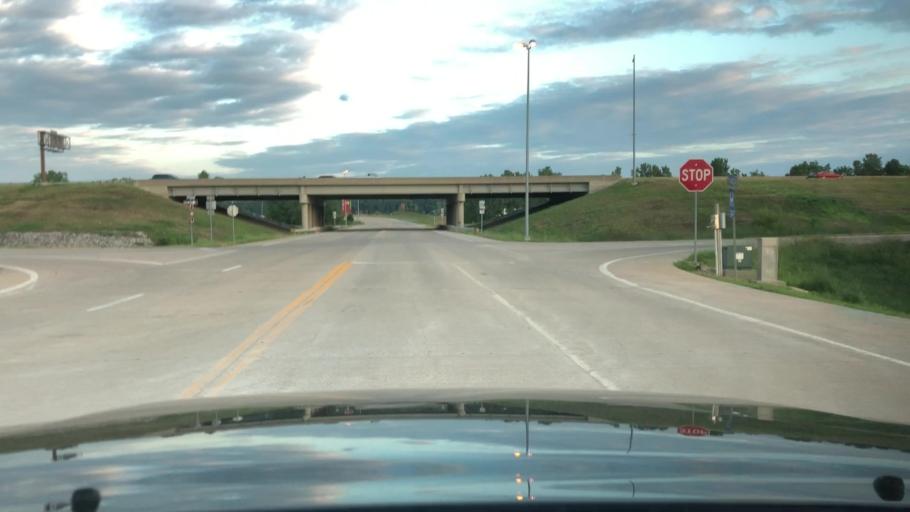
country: US
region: Missouri
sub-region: Saint Charles County
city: Saint Peters
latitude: 38.8189
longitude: -90.5616
